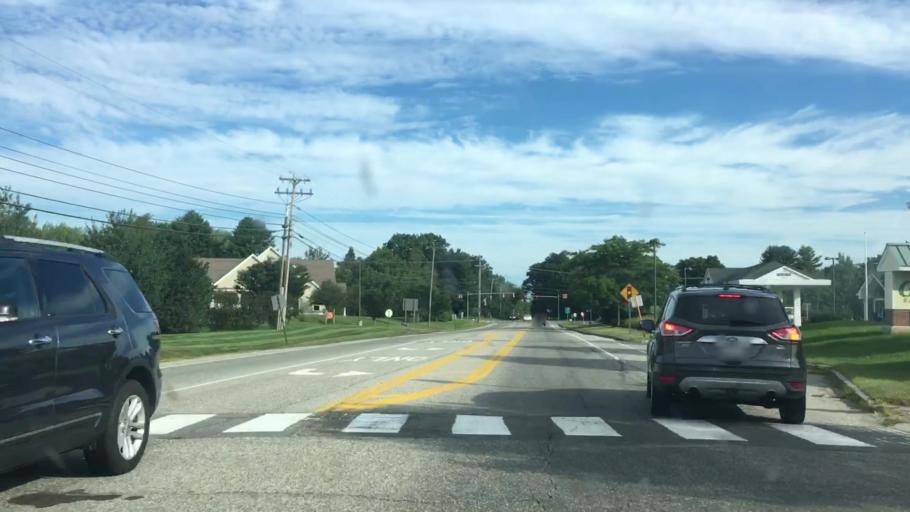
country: US
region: Maine
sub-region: Cumberland County
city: Falmouth
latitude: 43.7345
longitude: -70.2967
